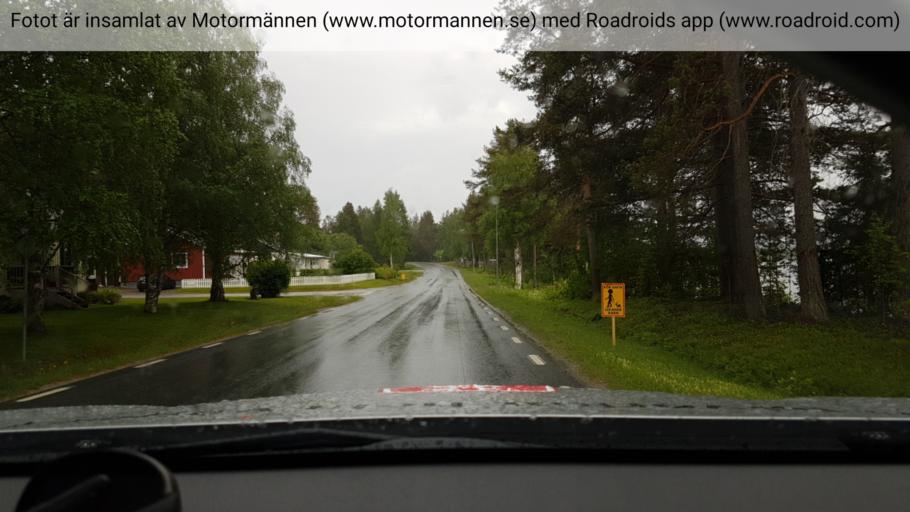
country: SE
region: Vaesterbotten
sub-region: Sorsele Kommun
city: Sorsele
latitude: 65.3383
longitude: 17.5897
